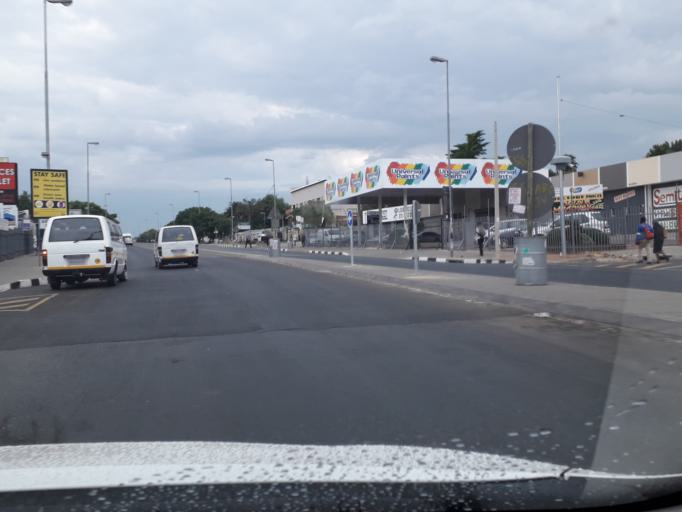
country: ZA
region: Gauteng
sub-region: City of Johannesburg Metropolitan Municipality
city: Johannesburg
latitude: -26.1269
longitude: 28.0851
